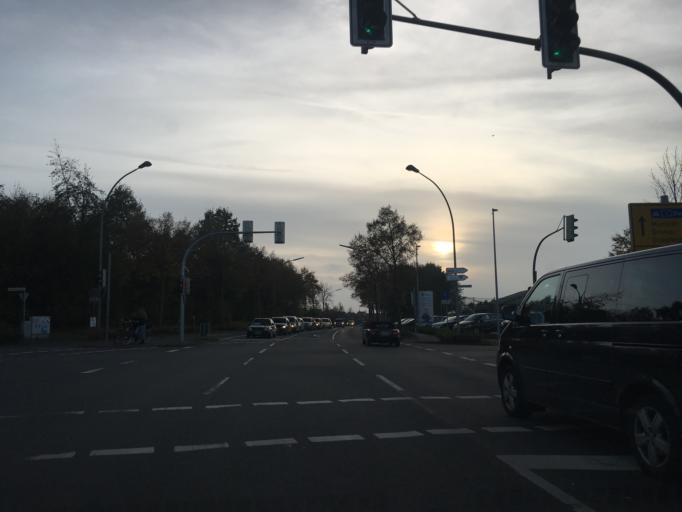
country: DE
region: North Rhine-Westphalia
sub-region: Regierungsbezirk Munster
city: Steinfurt
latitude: 52.1190
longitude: 7.3893
